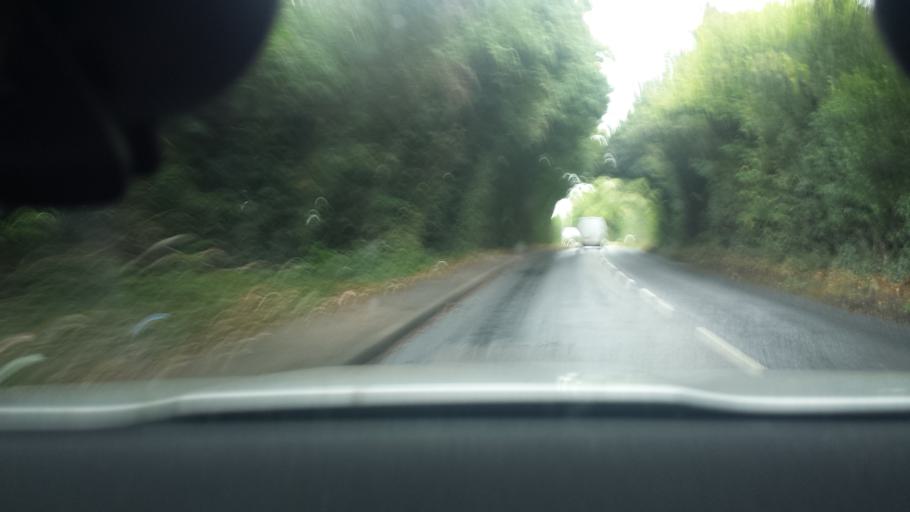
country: GB
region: England
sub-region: Kent
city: Harrietsham
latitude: 51.2373
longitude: 0.5994
